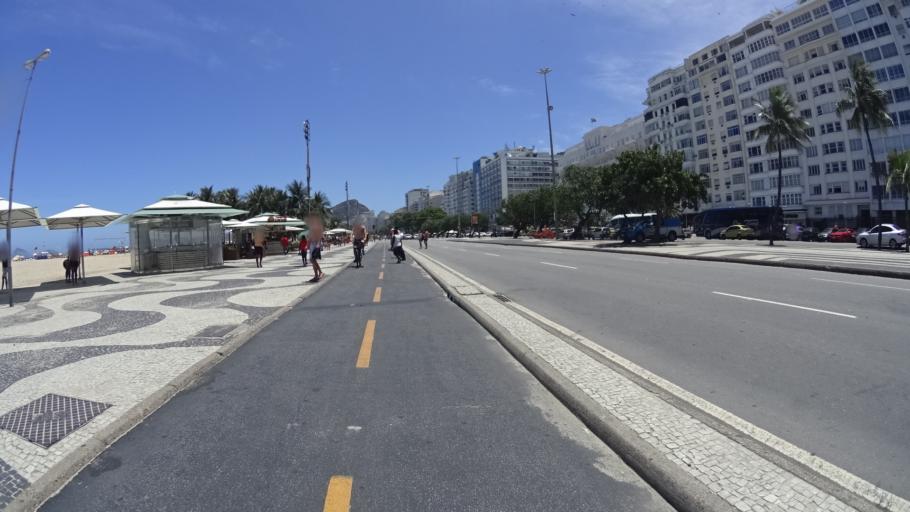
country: BR
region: Rio de Janeiro
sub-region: Rio De Janeiro
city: Rio de Janeiro
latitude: -22.9672
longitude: -43.1772
